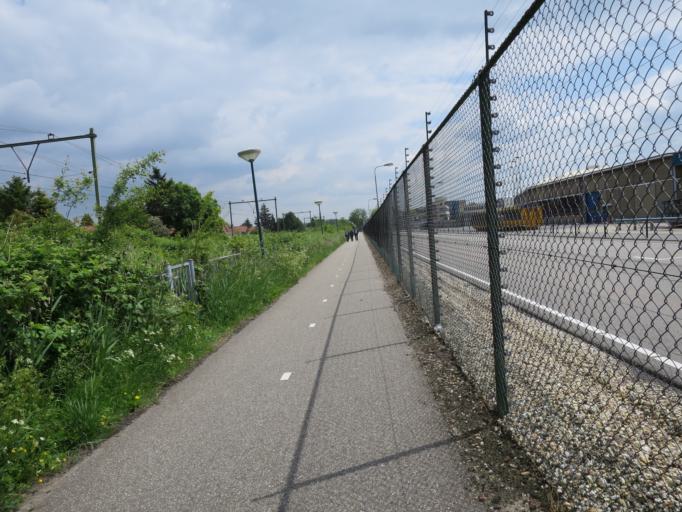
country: NL
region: Utrecht
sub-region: Gemeente Bunnik
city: Bunnik
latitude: 52.0636
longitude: 5.2019
